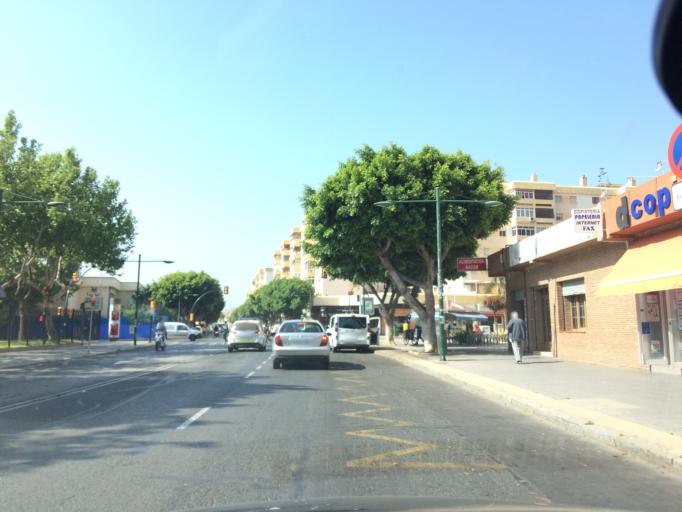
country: ES
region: Andalusia
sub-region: Provincia de Malaga
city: Malaga
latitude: 36.6913
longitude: -4.4466
